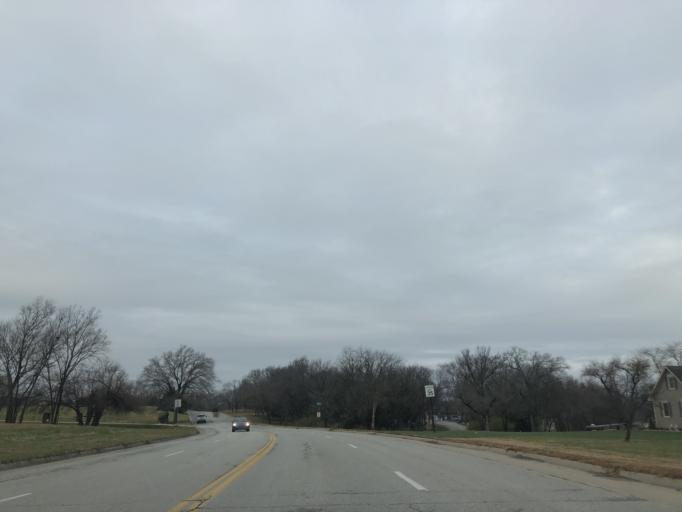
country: US
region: Kansas
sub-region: Johnson County
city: Gardner
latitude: 38.8491
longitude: -94.9311
